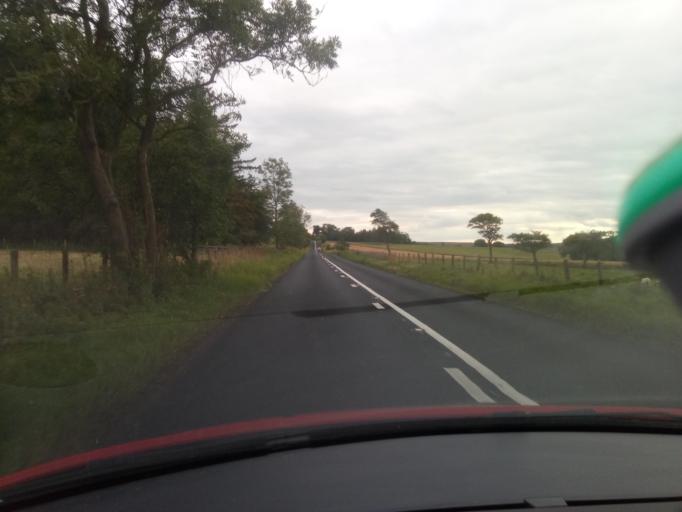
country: GB
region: England
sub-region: Northumberland
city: Warden
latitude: 54.9571
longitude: -2.1698
